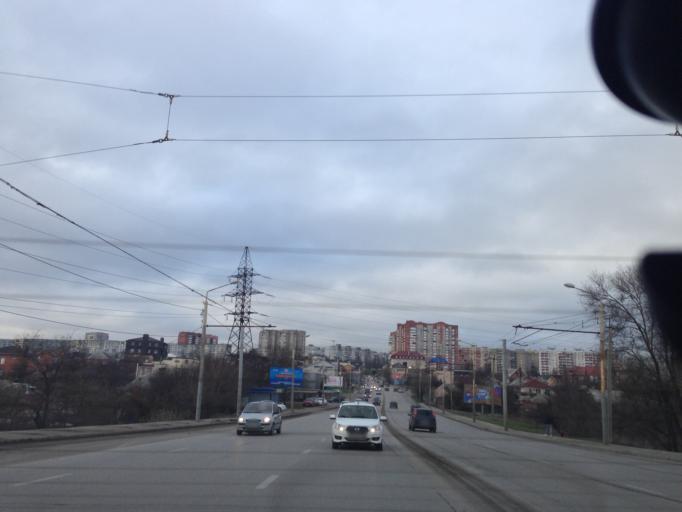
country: RU
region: Rostov
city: Temernik
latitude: 47.2934
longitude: 39.7309
